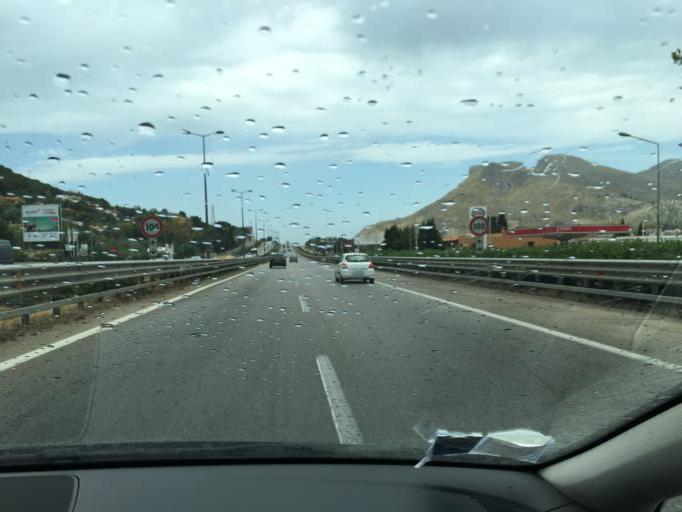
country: IT
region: Sicily
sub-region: Palermo
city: Isola delle Femmine
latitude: 38.1788
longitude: 13.2935
